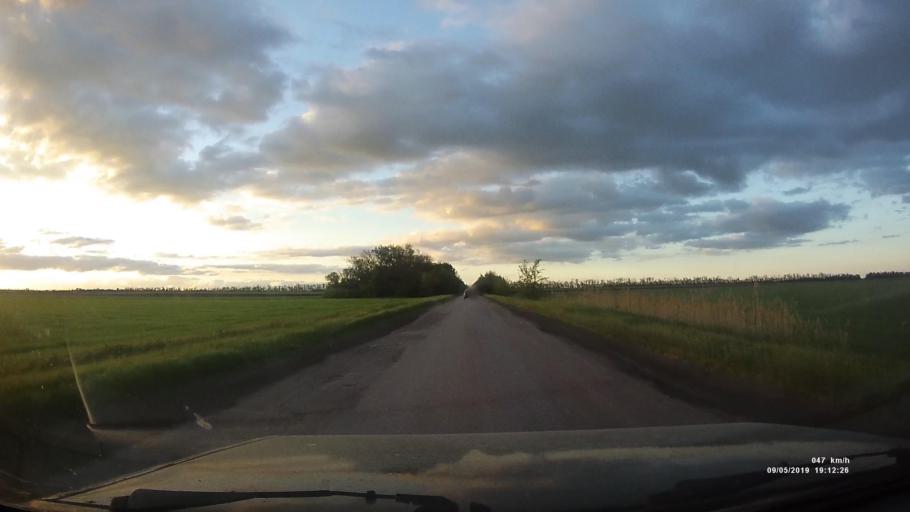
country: RU
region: Krasnodarskiy
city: Kanelovskaya
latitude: 46.7416
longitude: 39.2137
